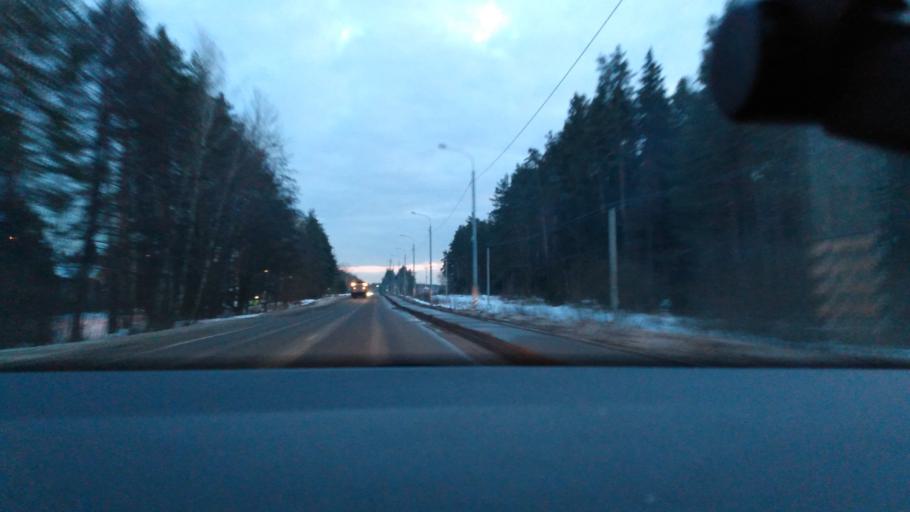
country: RU
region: Moskovskaya
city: Yegor'yevsk
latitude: 55.3559
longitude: 39.0724
